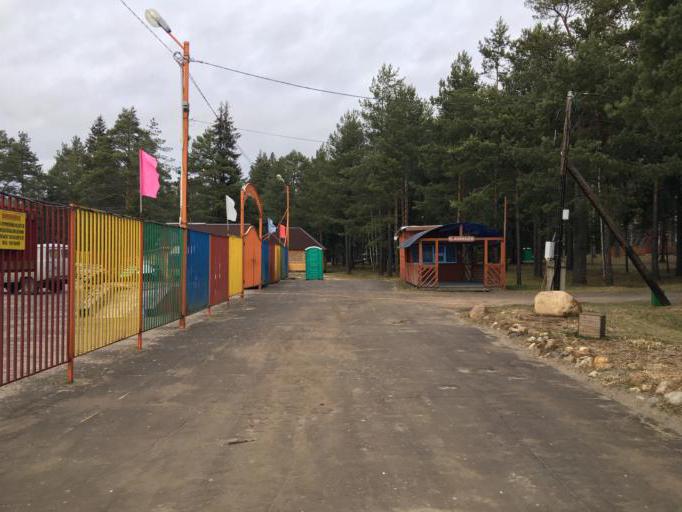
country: RU
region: Kostroma
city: Shar'ya
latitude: 58.3835
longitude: 45.4928
